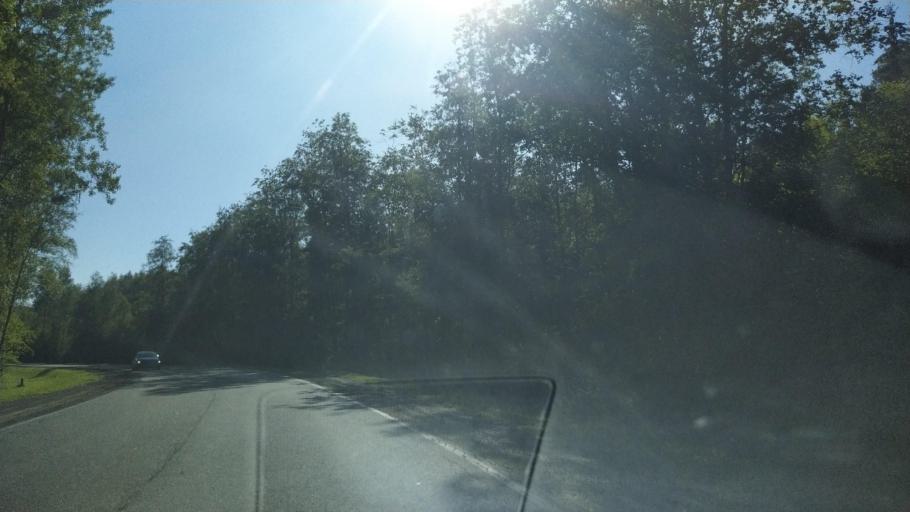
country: RU
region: Leningrad
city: Kirovsk
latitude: 59.9250
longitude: 30.9502
